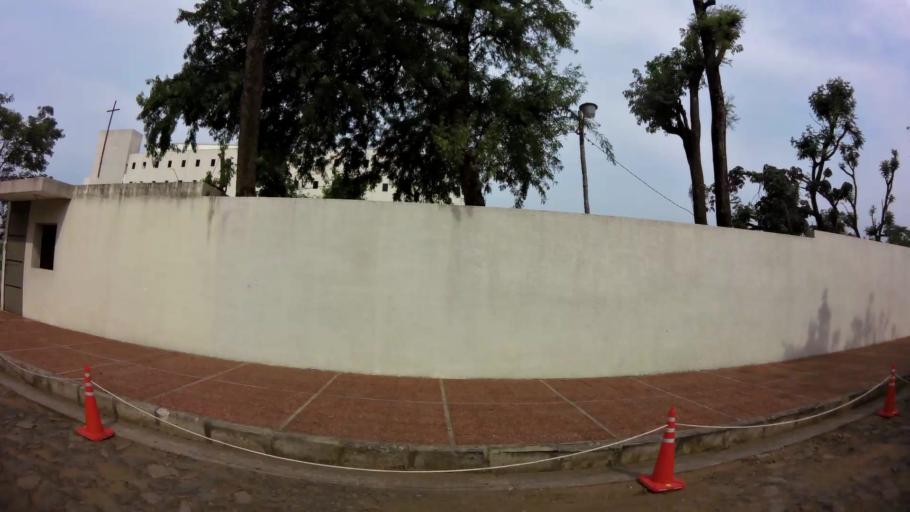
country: PY
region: Central
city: Fernando de la Mora
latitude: -25.3032
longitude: -57.5561
